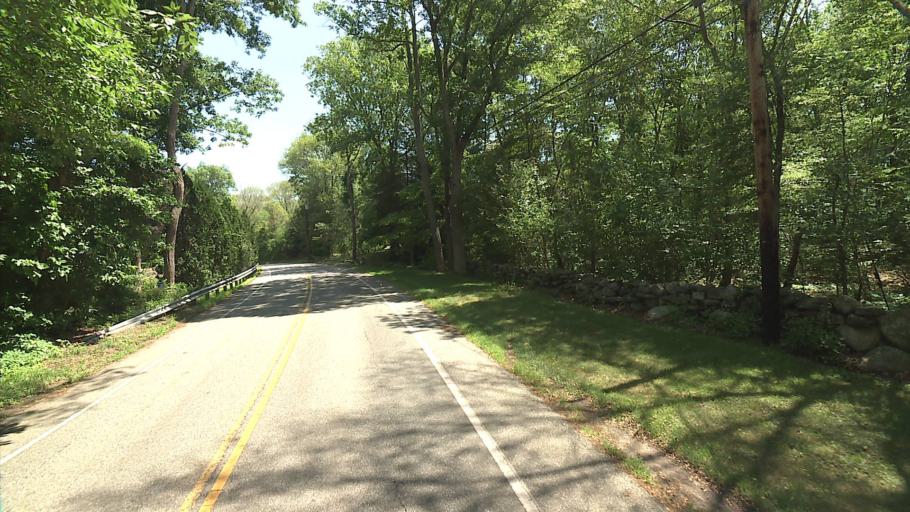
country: US
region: Connecticut
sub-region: New London County
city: Old Mystic
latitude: 41.4361
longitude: -71.9179
